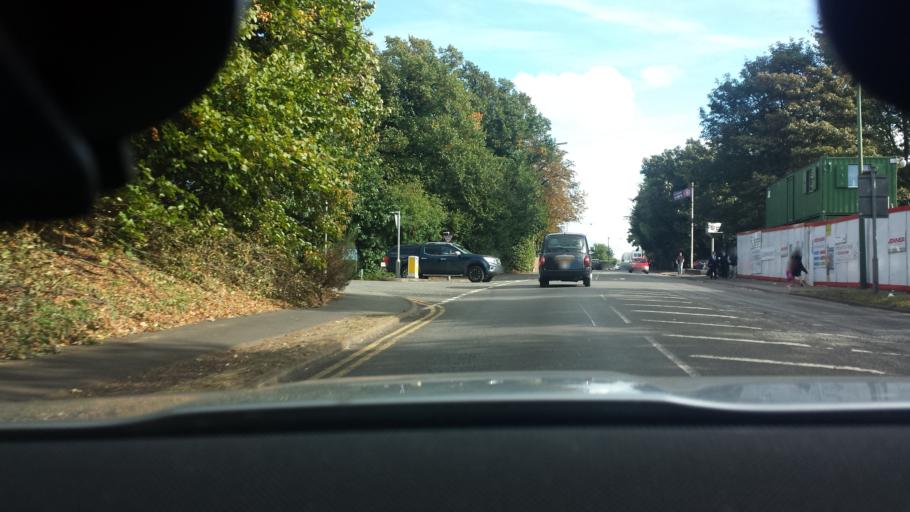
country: GB
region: England
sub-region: Kent
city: Swanley
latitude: 51.3988
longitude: 0.1706
